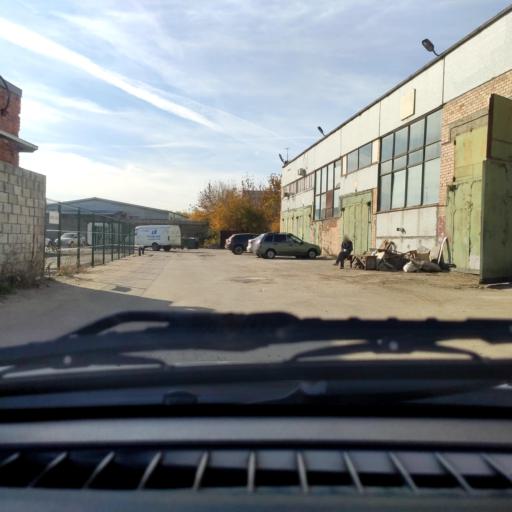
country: RU
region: Samara
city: Zhigulevsk
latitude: 53.5227
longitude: 49.4797
